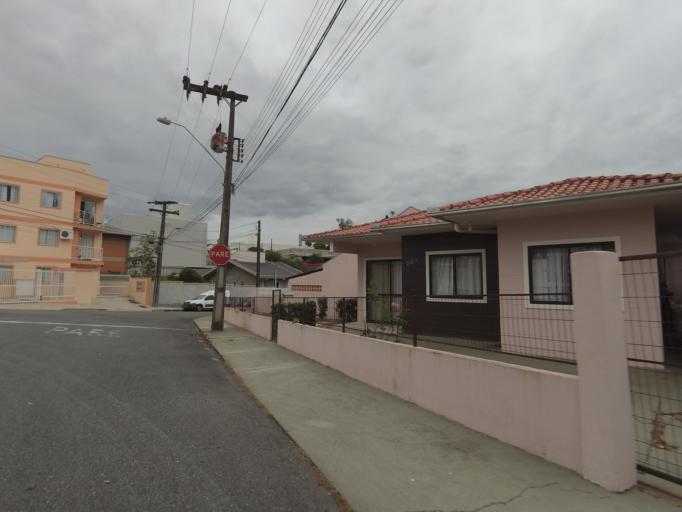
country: BR
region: Santa Catarina
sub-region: Blumenau
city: Blumenau
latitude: -26.8991
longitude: -49.1288
